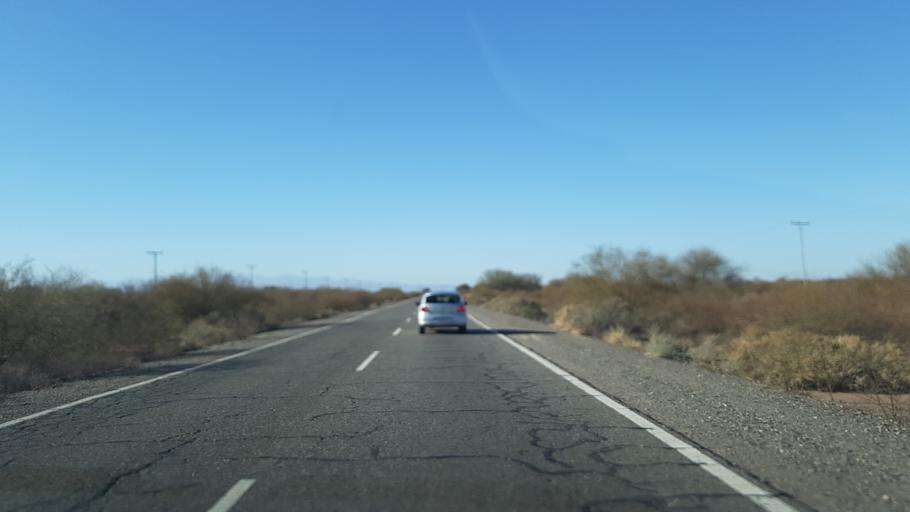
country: AR
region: San Juan
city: Caucete
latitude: -31.6139
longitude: -67.7252
